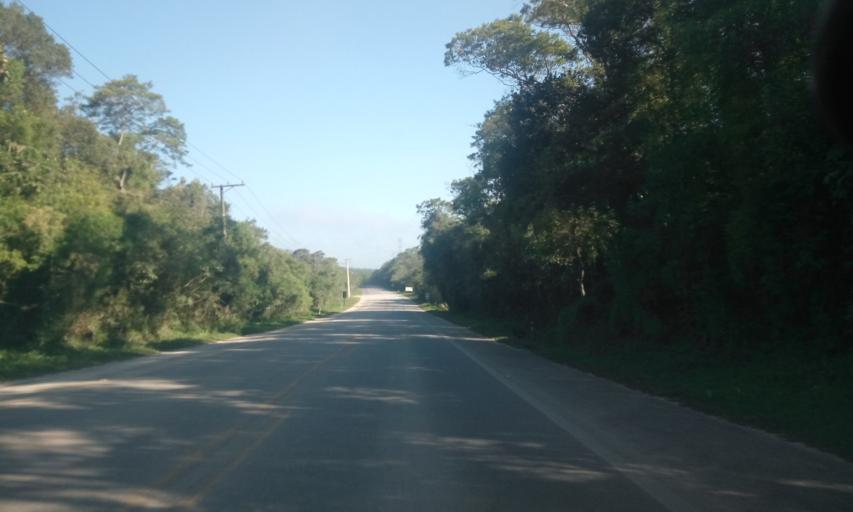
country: BR
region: Sao Paulo
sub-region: Cubatao
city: Cubatao
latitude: -23.8210
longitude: -46.4768
